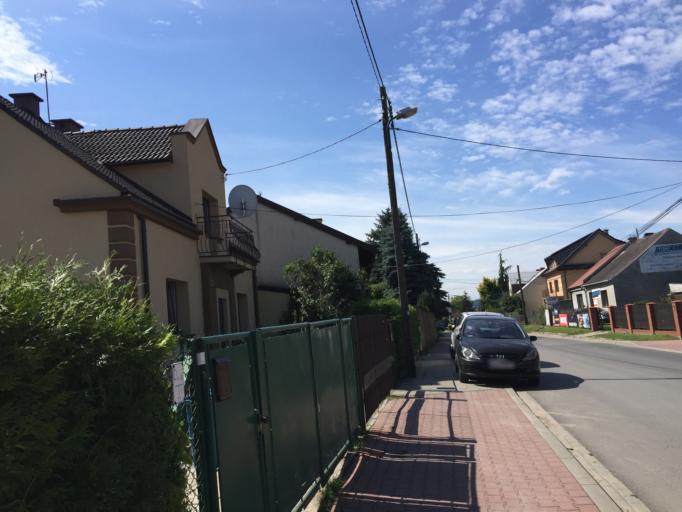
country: PL
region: Lesser Poland Voivodeship
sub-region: Powiat krakowski
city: Rzaska
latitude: 50.0877
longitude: 19.8820
